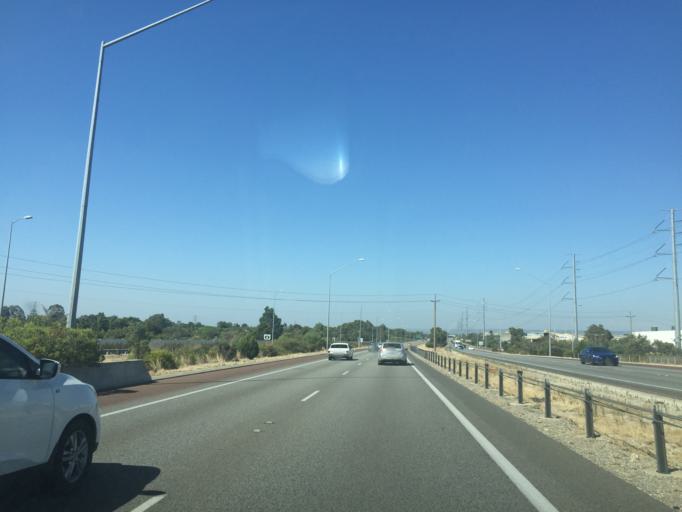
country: AU
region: Western Australia
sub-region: Canning
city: Willetton
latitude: -32.0678
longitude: 115.8914
